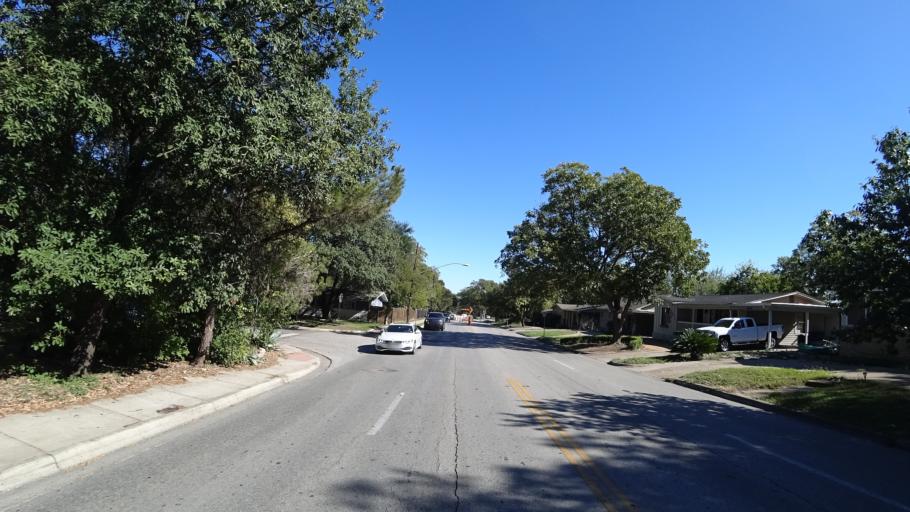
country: US
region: Texas
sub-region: Travis County
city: Austin
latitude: 30.3202
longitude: -97.7518
